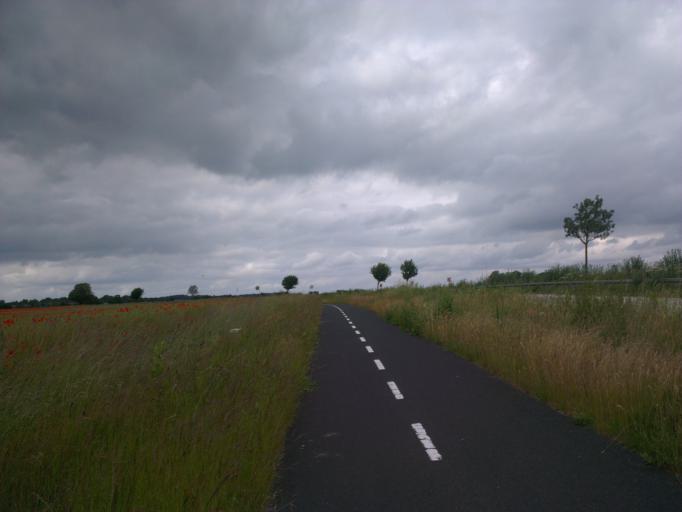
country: DK
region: Capital Region
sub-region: Frederikssund Kommune
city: Skibby
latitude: 55.6914
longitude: 11.9500
